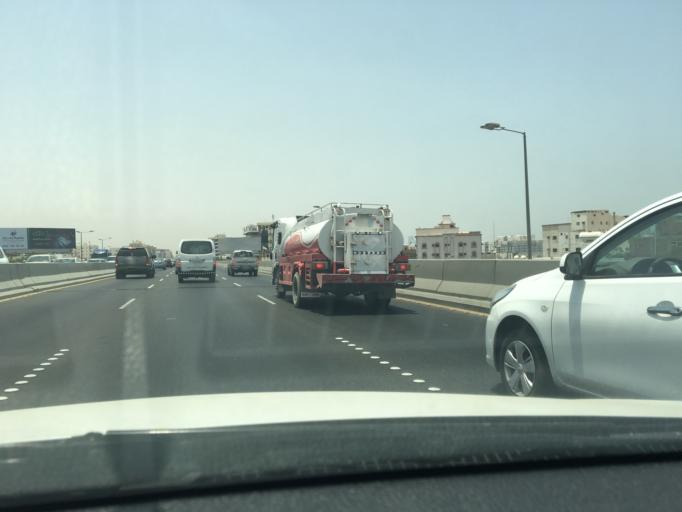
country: SA
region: Makkah
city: Jeddah
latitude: 21.5460
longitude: 39.1901
